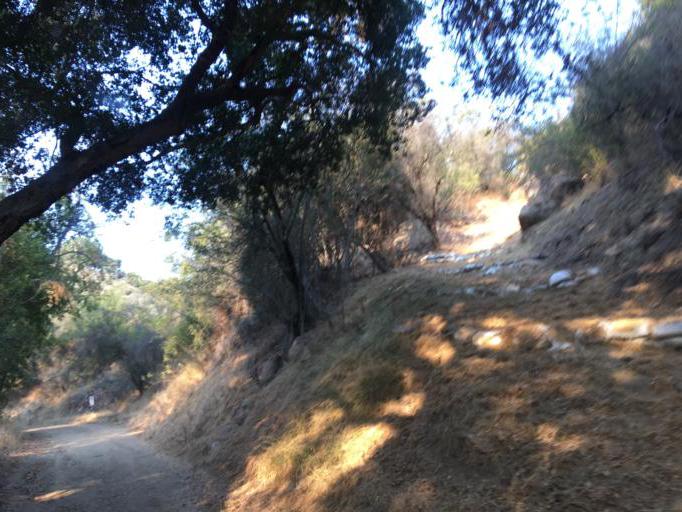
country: US
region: California
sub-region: Los Angeles County
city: Topanga
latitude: 34.0719
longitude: -118.6023
